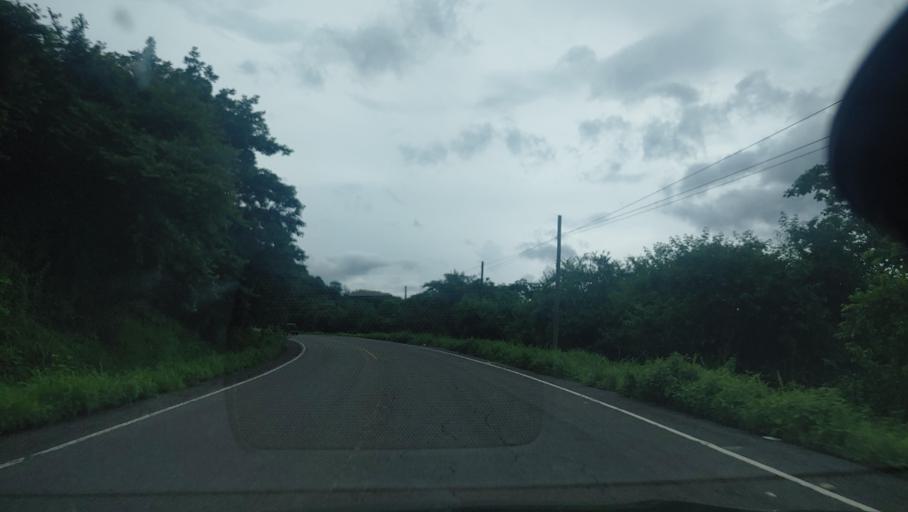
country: HN
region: Choluteca
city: Santa Ana de Yusguare
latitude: 13.3689
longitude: -87.0772
